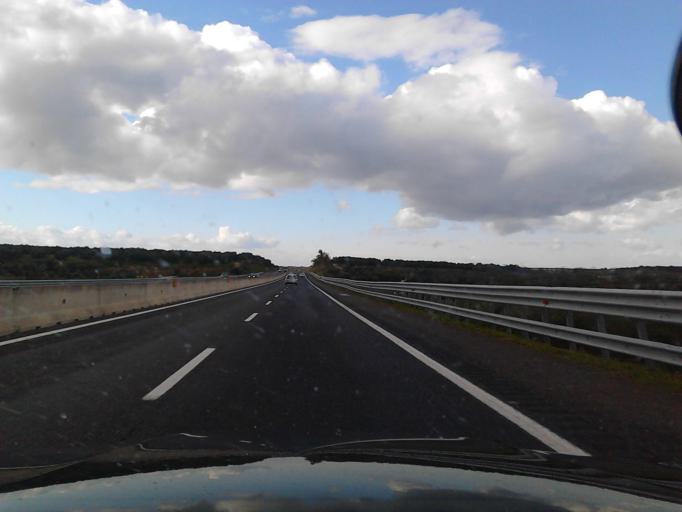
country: IT
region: Apulia
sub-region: Provincia di Barletta - Andria - Trani
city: Andria
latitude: 41.2607
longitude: 16.2623
